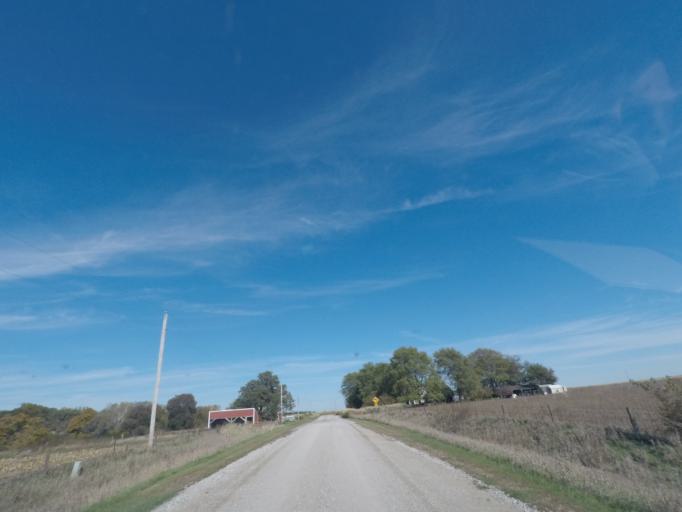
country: US
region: Iowa
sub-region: Story County
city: Nevada
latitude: 42.0431
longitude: -93.3596
